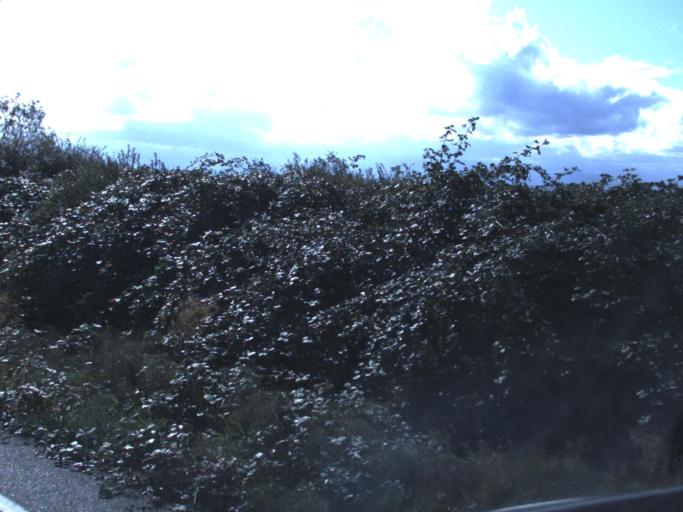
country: US
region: Washington
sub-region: Island County
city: Coupeville
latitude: 48.1701
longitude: -122.6375
